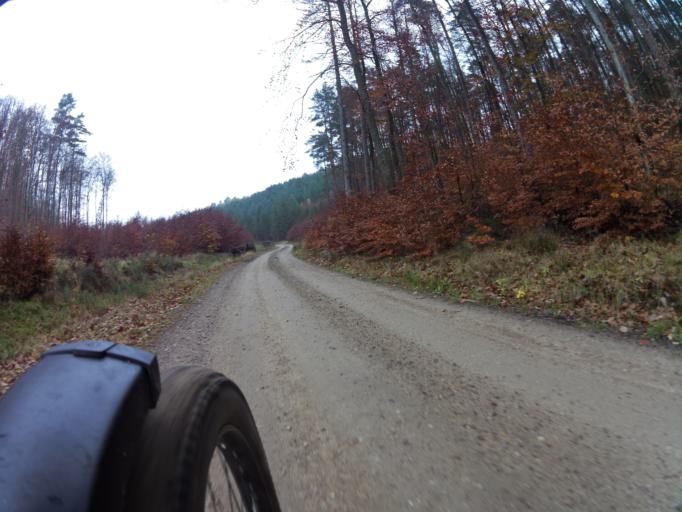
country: PL
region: Pomeranian Voivodeship
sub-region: Powiat wejherowski
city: Orle
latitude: 54.7071
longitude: 18.1463
